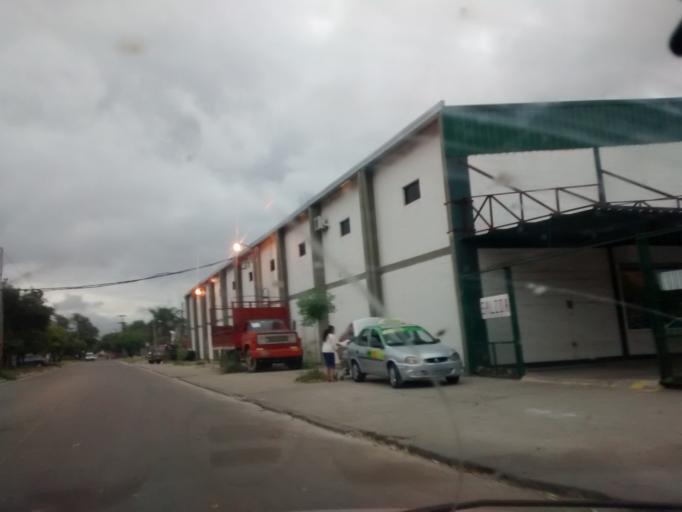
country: AR
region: Chaco
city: Resistencia
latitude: -27.4480
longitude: -59.0119
